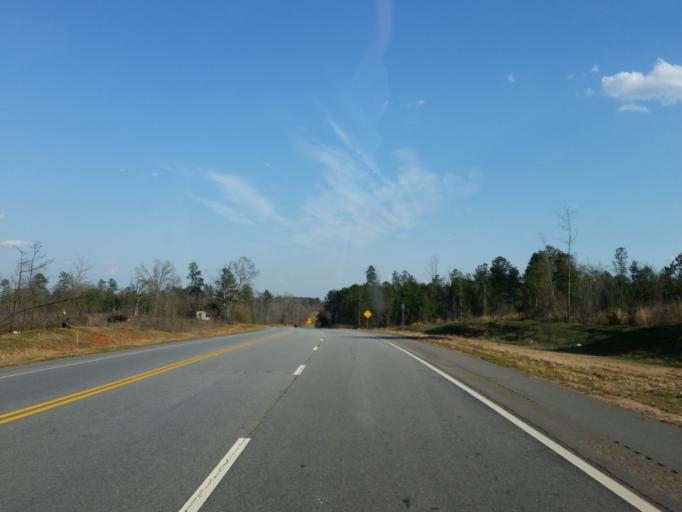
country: US
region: Georgia
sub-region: Monroe County
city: Forsyth
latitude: 33.0364
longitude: -83.9992
